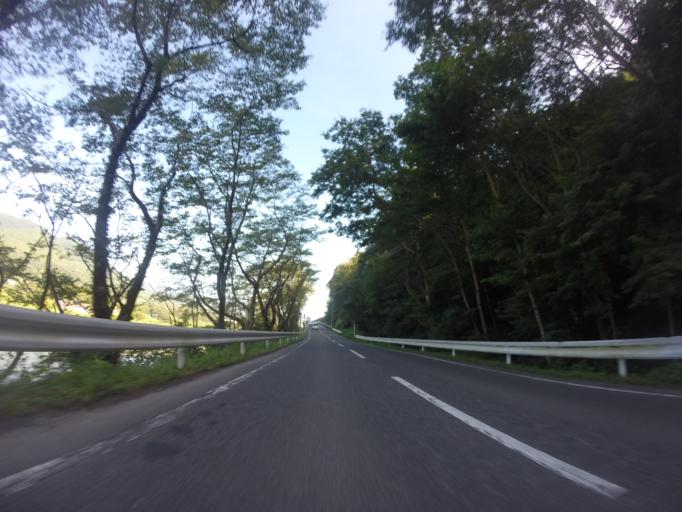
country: JP
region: Shizuoka
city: Fujinomiya
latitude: 35.2973
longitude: 138.4564
